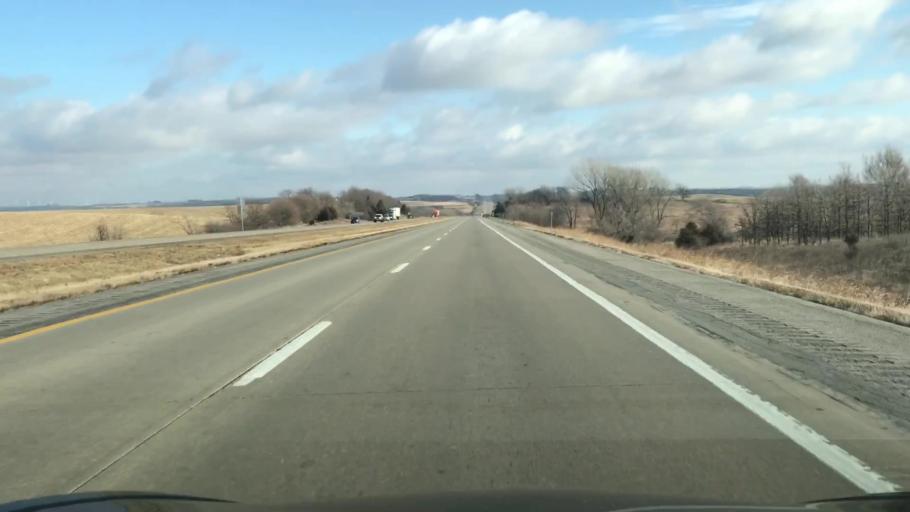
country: US
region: Iowa
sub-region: Cass County
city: Atlantic
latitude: 41.4973
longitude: -94.8823
